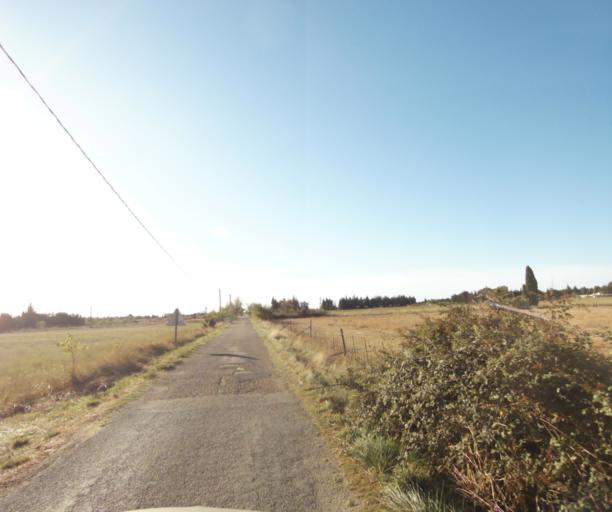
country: FR
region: Languedoc-Roussillon
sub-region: Departement du Gard
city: Bouillargues
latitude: 43.7868
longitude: 4.4494
